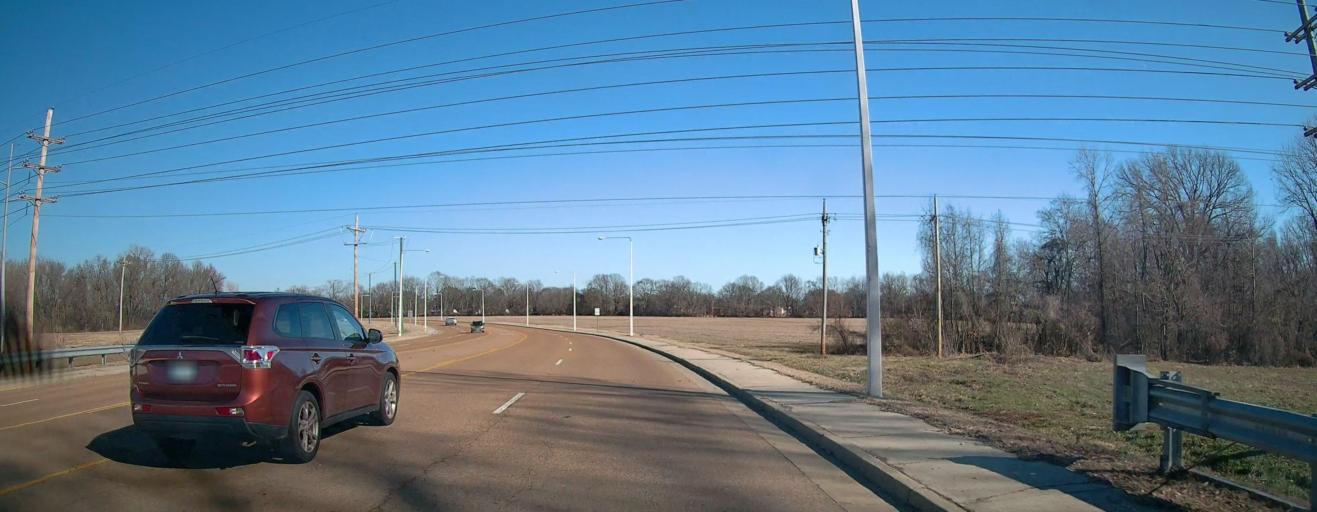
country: US
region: Tennessee
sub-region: Shelby County
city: Millington
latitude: 35.3364
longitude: -89.8928
